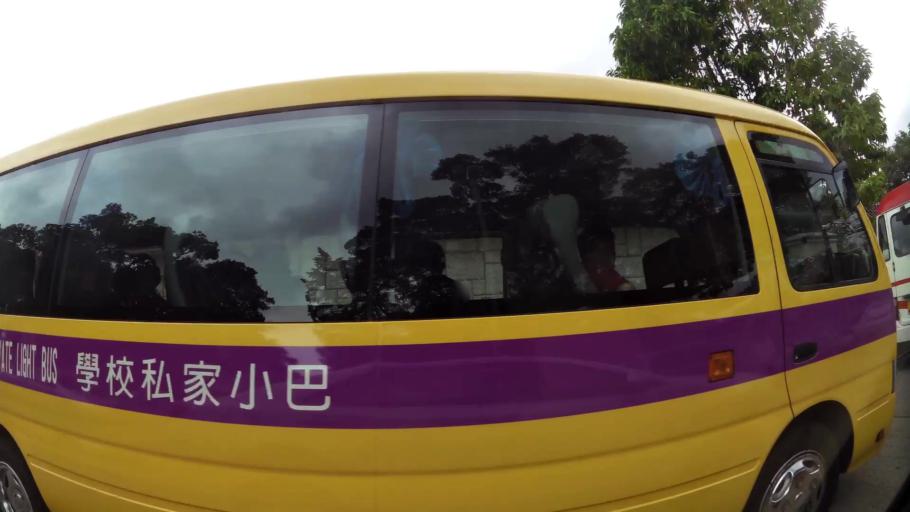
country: HK
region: Kowloon City
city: Kowloon
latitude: 22.3286
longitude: 114.1775
